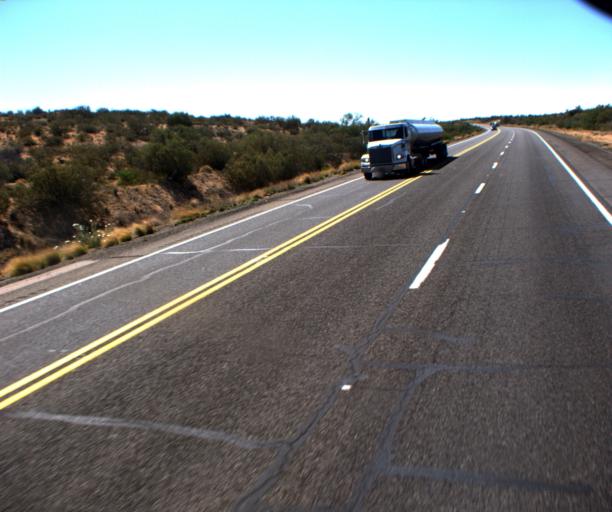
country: US
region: Arizona
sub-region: Yavapai County
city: Congress
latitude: 34.2003
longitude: -113.0613
